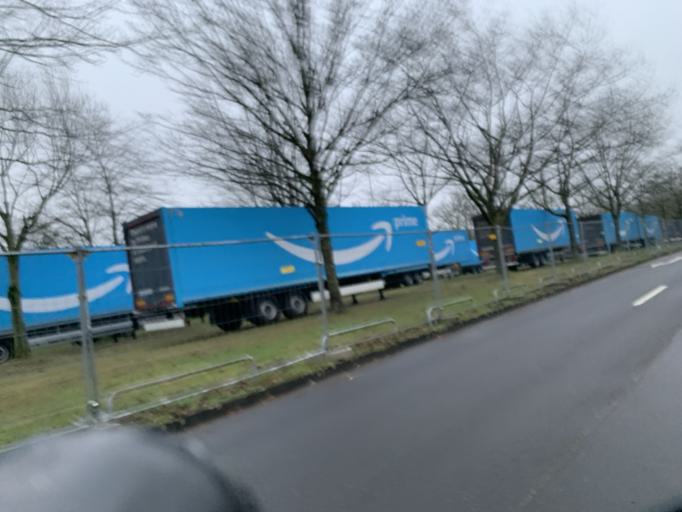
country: DE
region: North Rhine-Westphalia
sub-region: Regierungsbezirk Dusseldorf
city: Meerbusch
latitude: 51.2667
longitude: 6.7169
